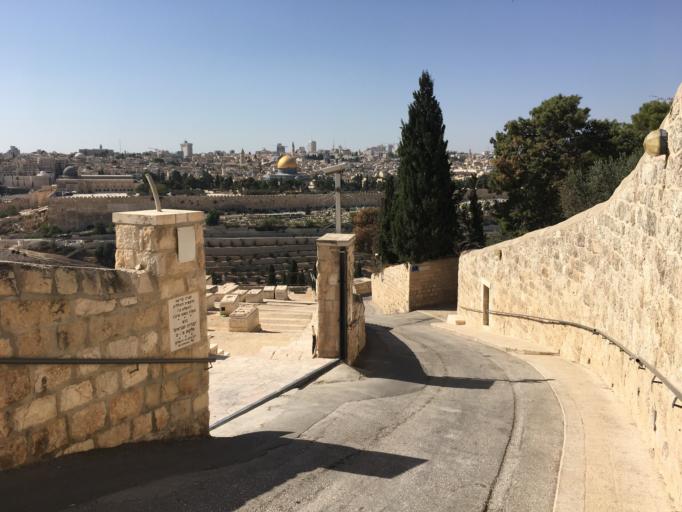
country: PS
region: West Bank
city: Old City
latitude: 31.7772
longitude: 35.2426
